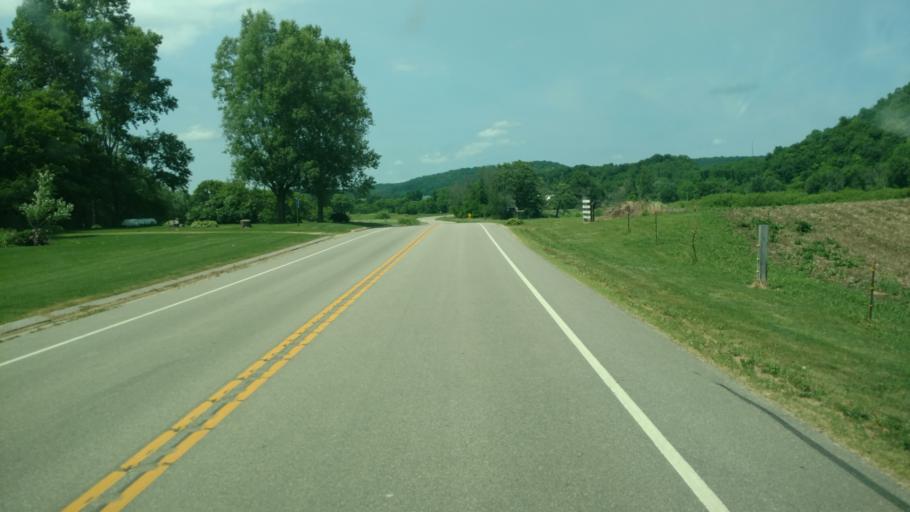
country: US
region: Wisconsin
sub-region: Vernon County
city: Westby
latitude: 43.5432
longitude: -90.6664
